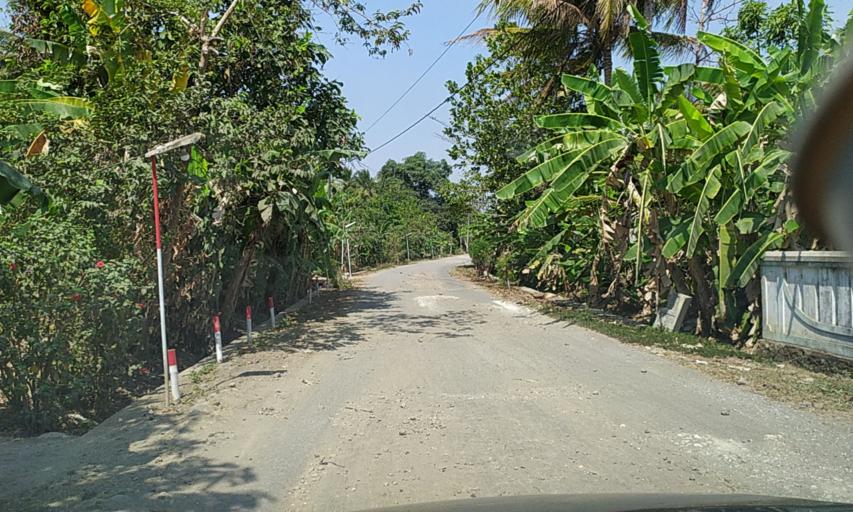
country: ID
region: Central Java
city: Mulyosari
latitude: -7.5025
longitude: 108.7922
